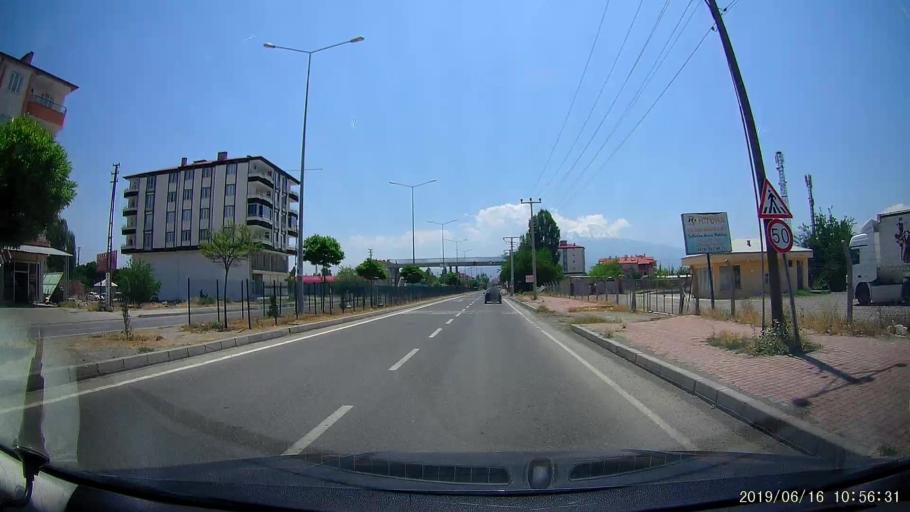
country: TR
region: Igdir
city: Igdir
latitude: 39.9289
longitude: 44.0238
